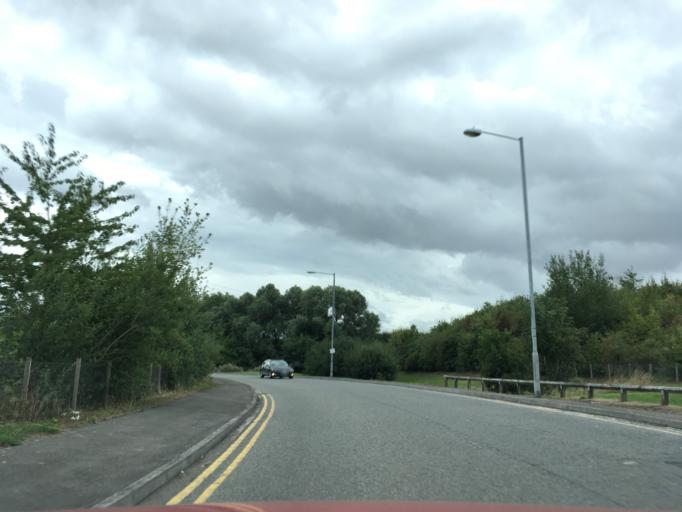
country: GB
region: Wales
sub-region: Monmouthshire
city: Chepstow
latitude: 51.6161
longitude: -2.6807
